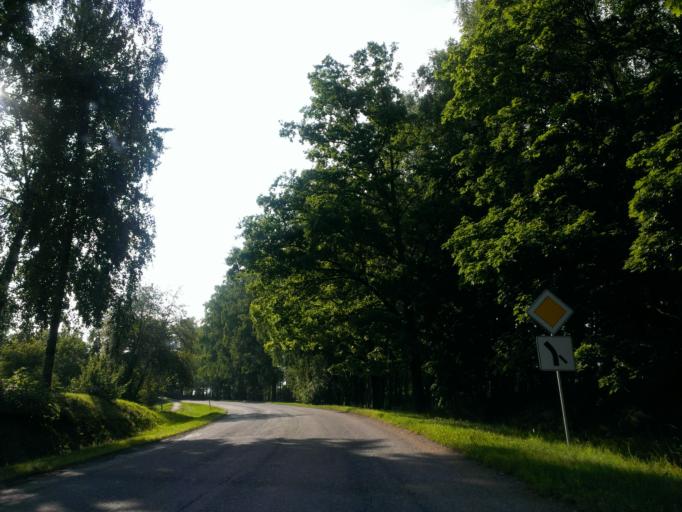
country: LV
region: Priekuli
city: Priekuli
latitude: 57.3159
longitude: 25.3704
